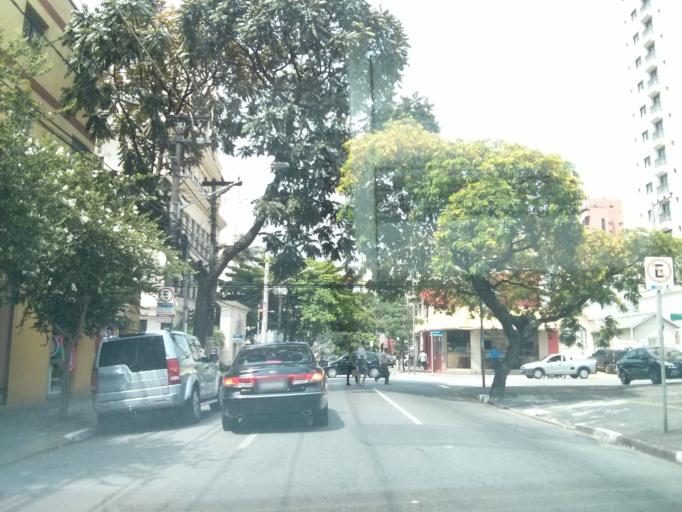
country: BR
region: Sao Paulo
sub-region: Sao Paulo
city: Sao Paulo
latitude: -23.6089
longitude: -46.6609
